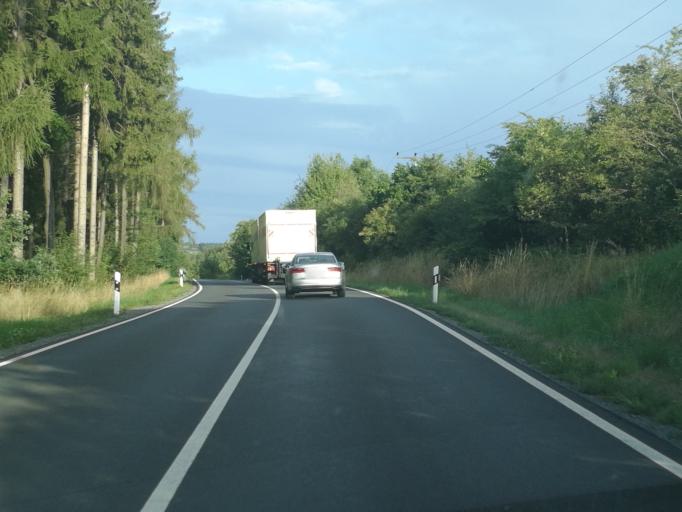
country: DE
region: Saxony
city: Eichigt
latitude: 50.3362
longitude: 12.2113
